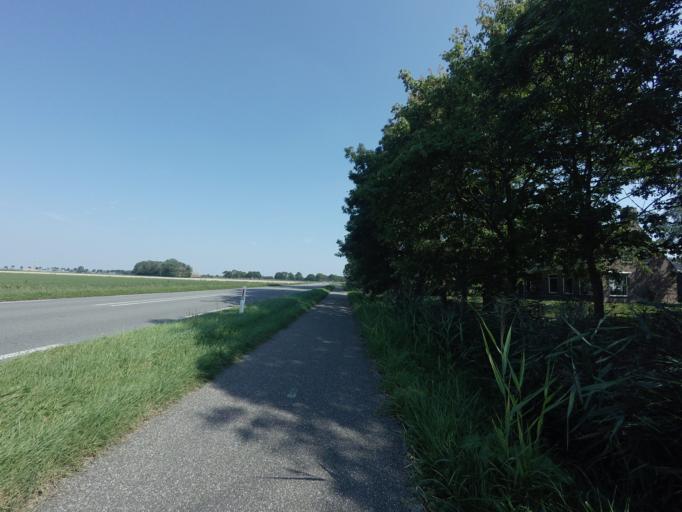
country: NL
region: Groningen
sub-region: Gemeente Zuidhorn
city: Noordhorn
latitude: 53.2638
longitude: 6.3768
